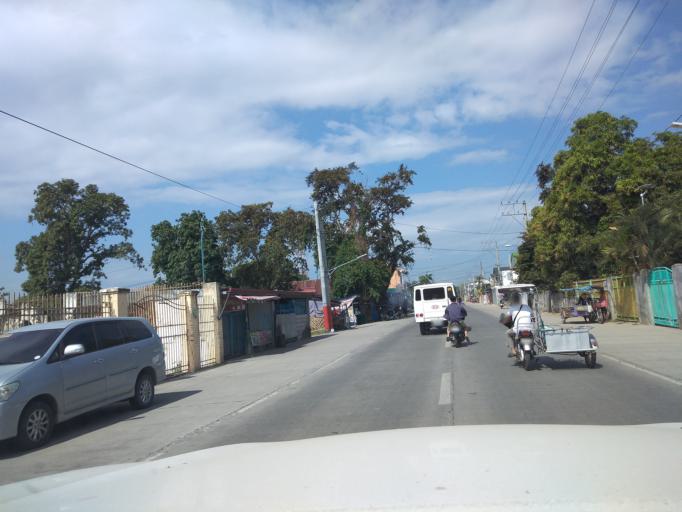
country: PH
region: Central Luzon
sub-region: Province of Pampanga
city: Candaba
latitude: 15.0946
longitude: 120.8218
